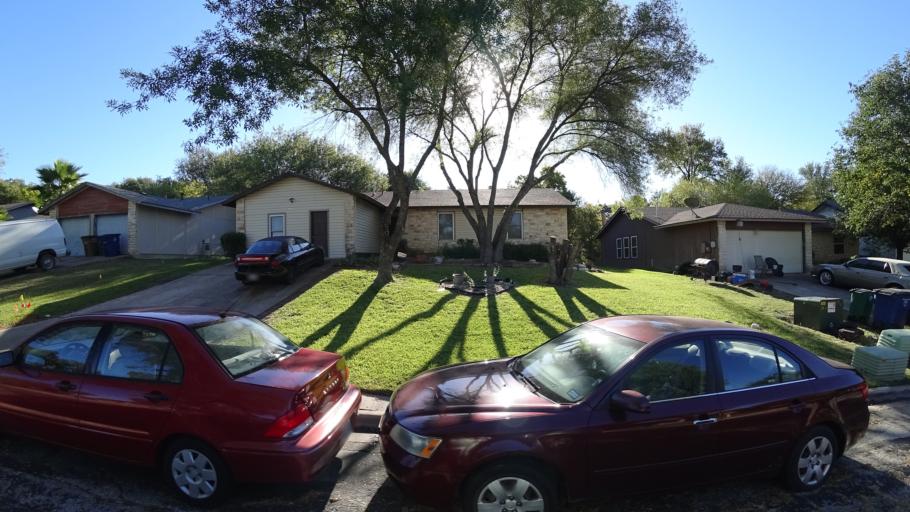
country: US
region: Texas
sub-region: Travis County
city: Austin
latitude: 30.3033
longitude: -97.6656
